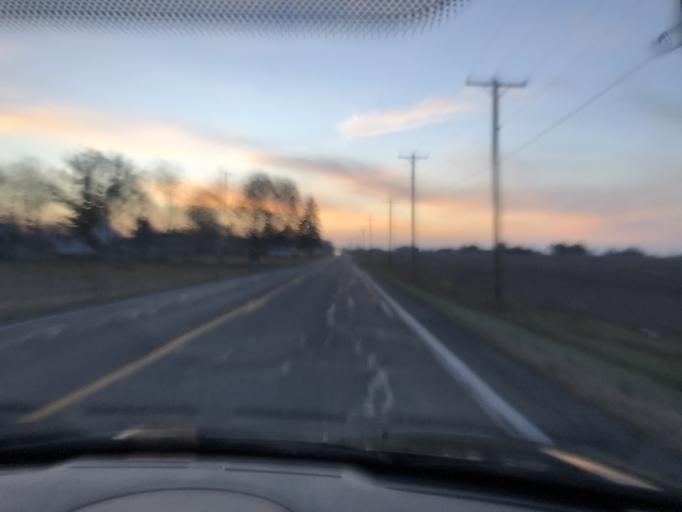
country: US
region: Ohio
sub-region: Champaign County
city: Urbana
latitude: 40.1083
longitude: -83.7042
